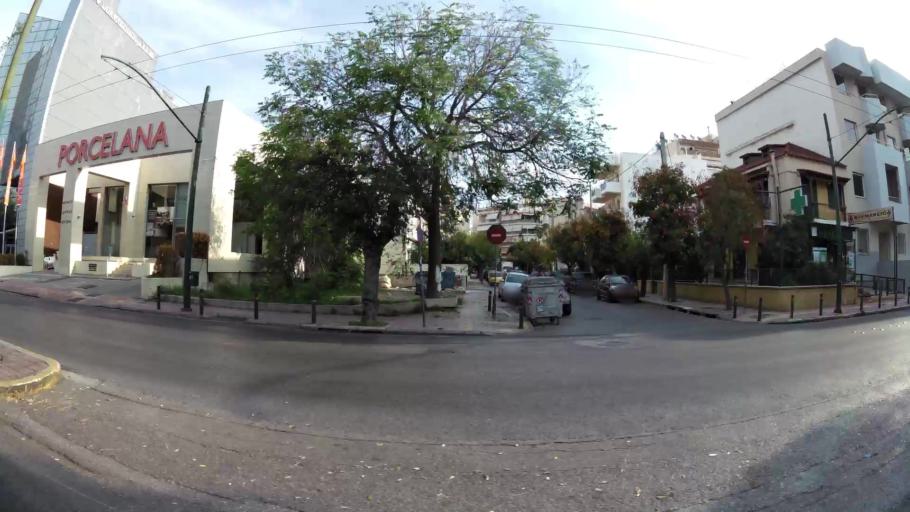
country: GR
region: Attica
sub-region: Nomarchia Athinas
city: Athens
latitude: 37.9968
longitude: 23.7112
